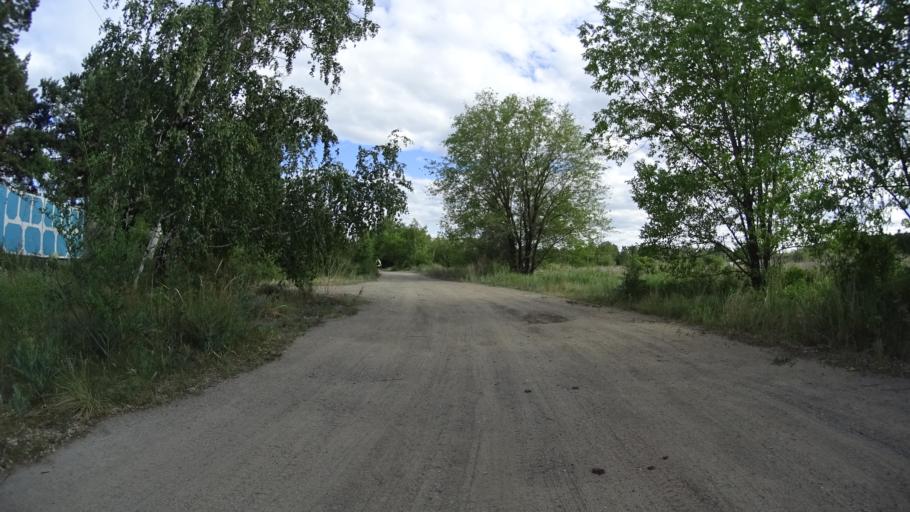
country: RU
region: Chelyabinsk
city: Troitsk
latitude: 54.0512
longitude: 61.6264
